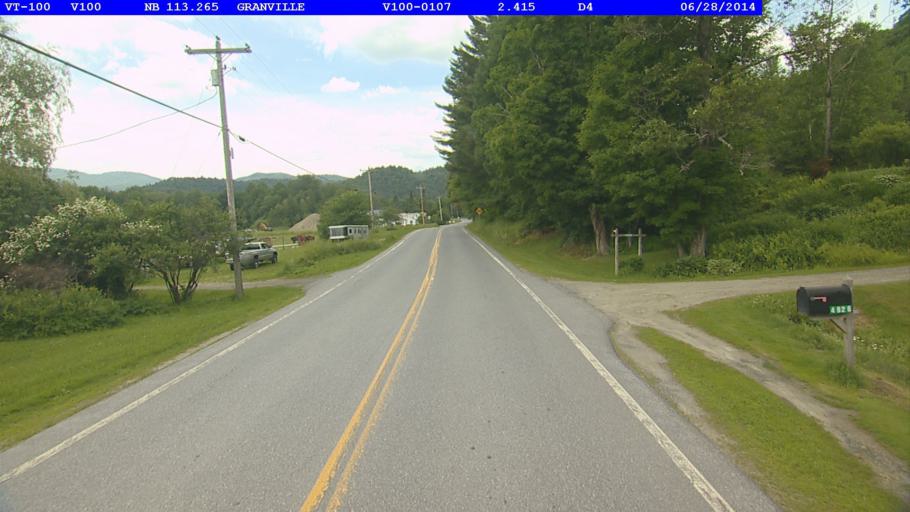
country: US
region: Vermont
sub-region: Orange County
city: Randolph
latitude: 43.9790
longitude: -72.8423
